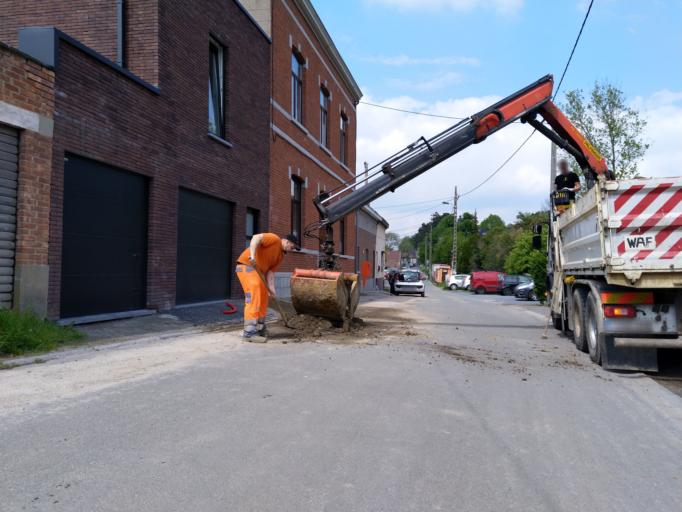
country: BE
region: Wallonia
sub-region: Province du Hainaut
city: Chasse Royale
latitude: 50.4368
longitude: 3.9686
